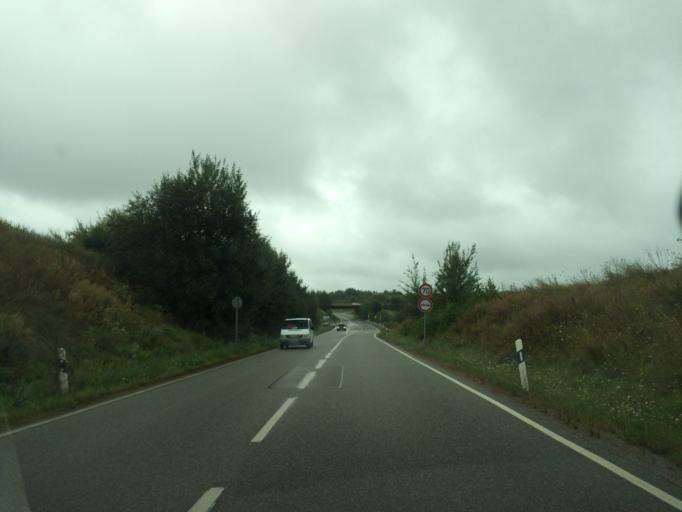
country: DE
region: Rheinland-Pfalz
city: Obersimten
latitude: 49.1926
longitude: 7.5777
